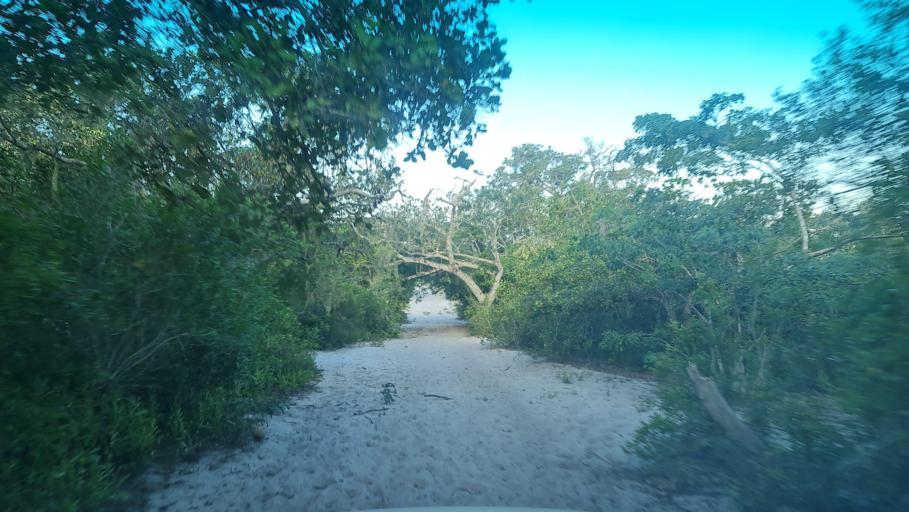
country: MZ
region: Gaza
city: Macia
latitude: -25.2274
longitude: 33.0216
